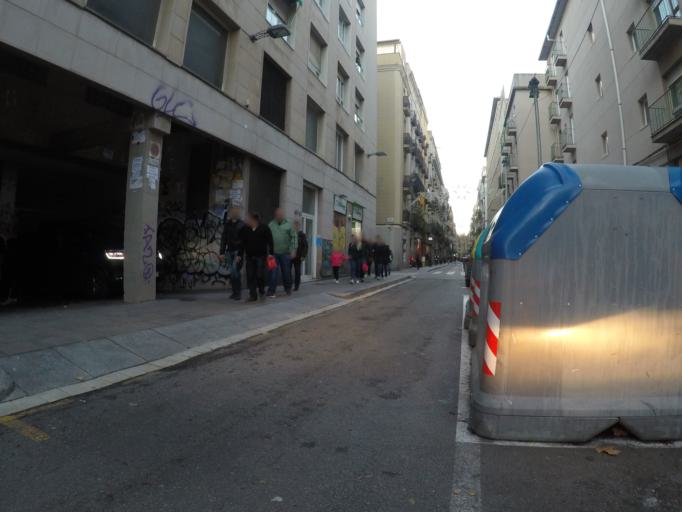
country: ES
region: Catalonia
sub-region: Provincia de Barcelona
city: Ciutat Vella
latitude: 41.3773
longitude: 2.1724
